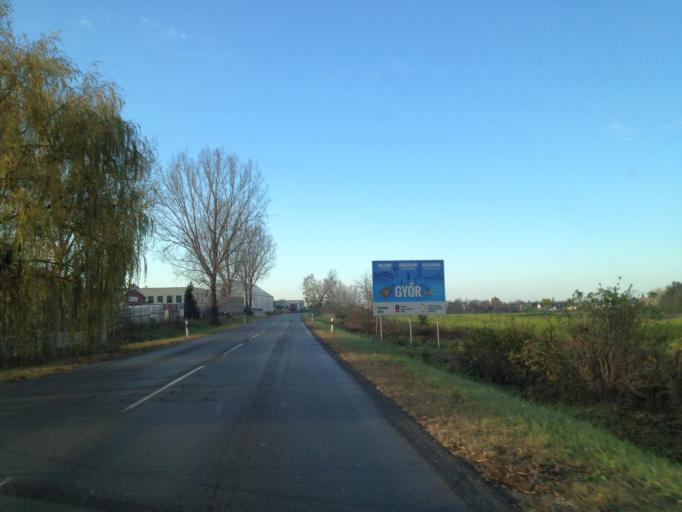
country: HU
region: Gyor-Moson-Sopron
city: Gyorujbarat
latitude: 47.6450
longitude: 17.6611
